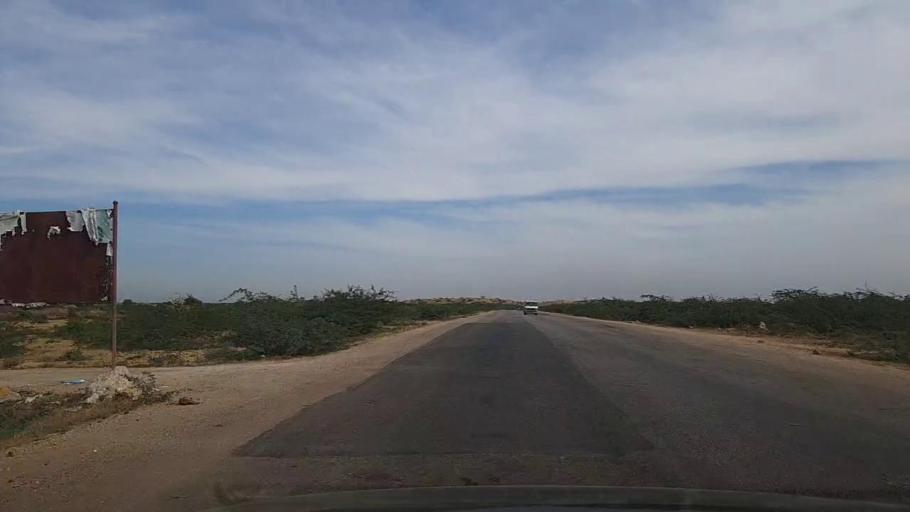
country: PK
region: Sindh
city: Daro Mehar
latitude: 24.8760
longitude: 68.0432
